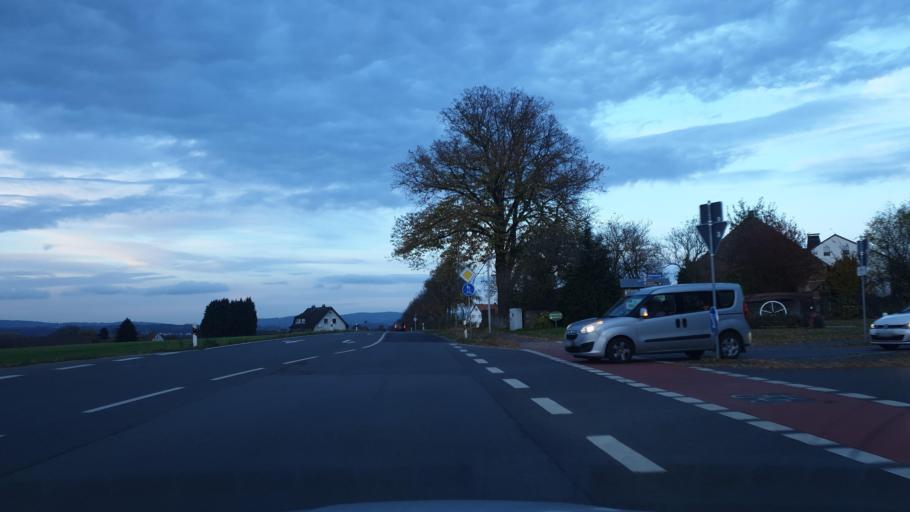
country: DE
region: North Rhine-Westphalia
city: Spenge
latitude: 52.1618
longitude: 8.5018
